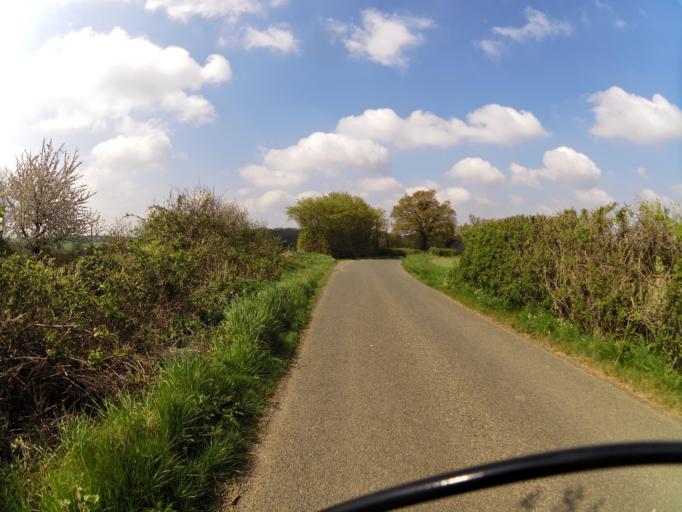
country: GB
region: England
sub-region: Suffolk
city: Hadleigh
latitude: 52.0770
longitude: 1.0205
